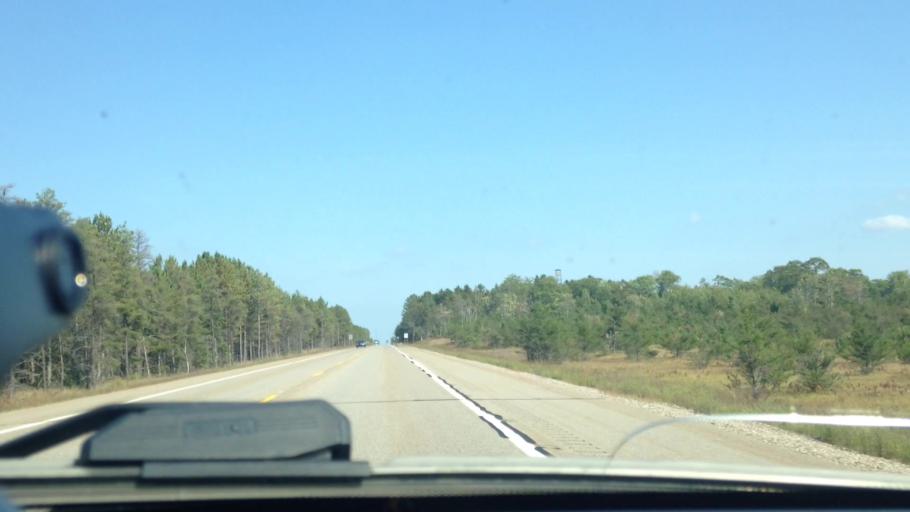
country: US
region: Michigan
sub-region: Chippewa County
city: Sault Ste. Marie
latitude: 46.3600
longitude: -84.7873
